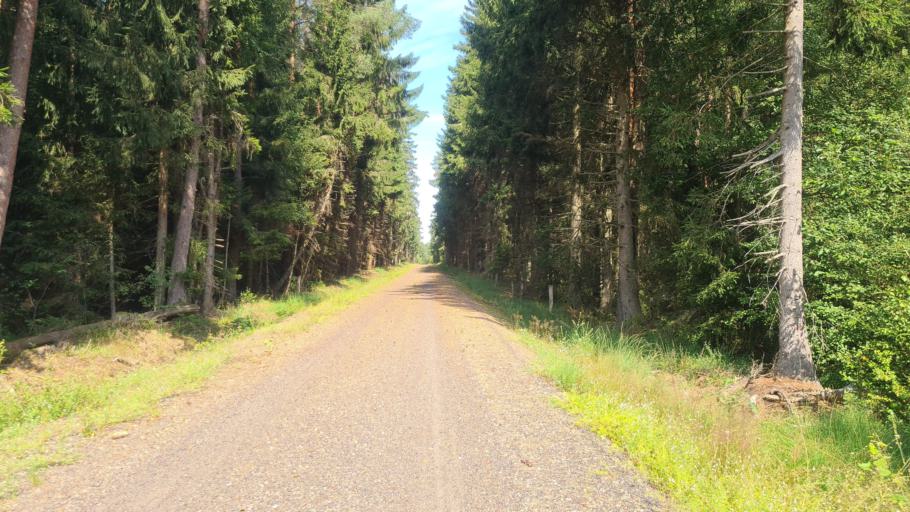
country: SE
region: Kronoberg
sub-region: Ljungby Kommun
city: Lagan
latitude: 56.9513
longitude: 13.9617
